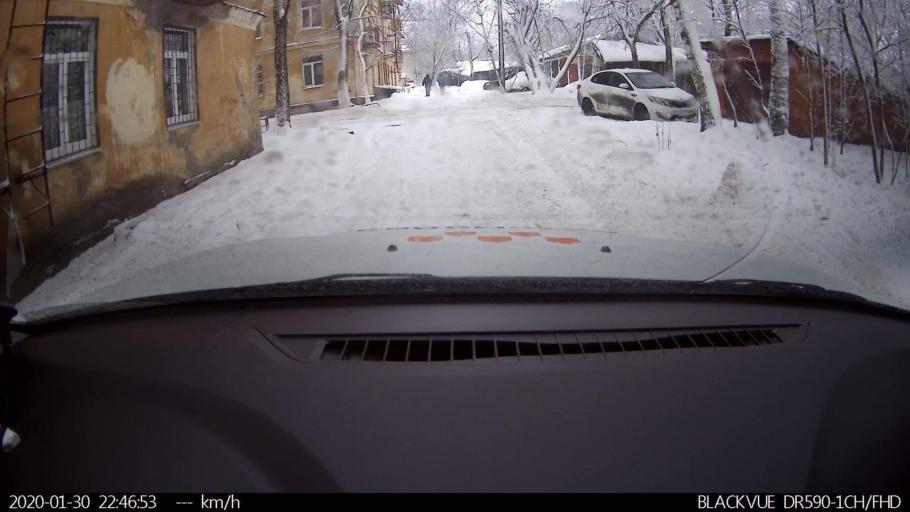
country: RU
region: Nizjnij Novgorod
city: Nizhniy Novgorod
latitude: 56.2824
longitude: 43.9856
